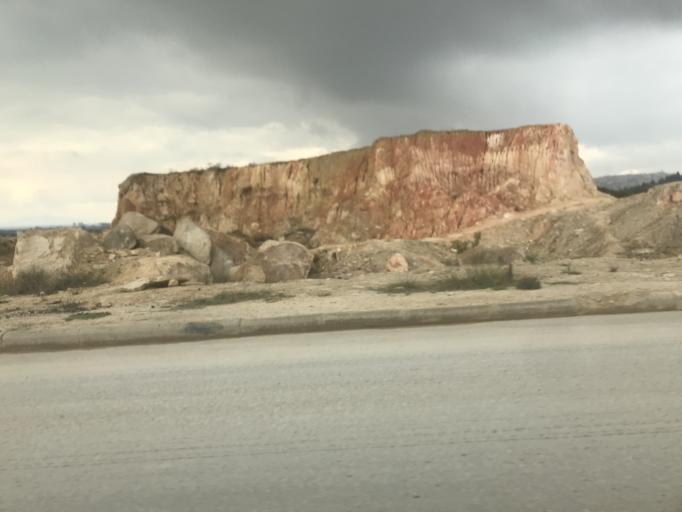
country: CO
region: Cundinamarca
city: Soacha
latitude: 4.5692
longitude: -74.2198
